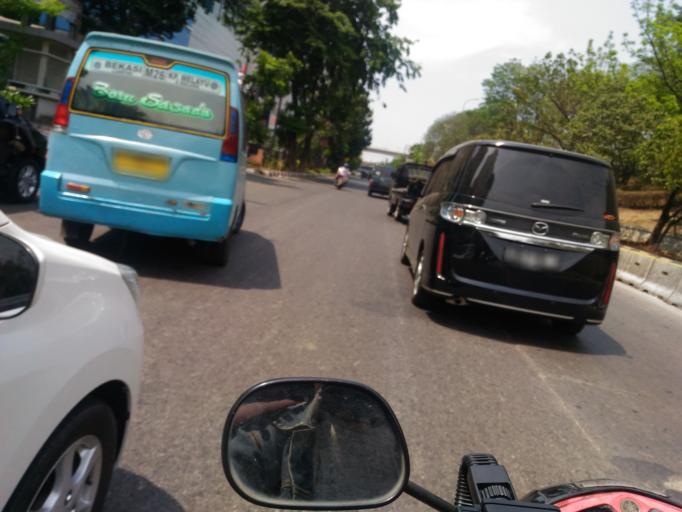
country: ID
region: Jakarta Raya
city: Jakarta
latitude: -6.2431
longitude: 106.8765
